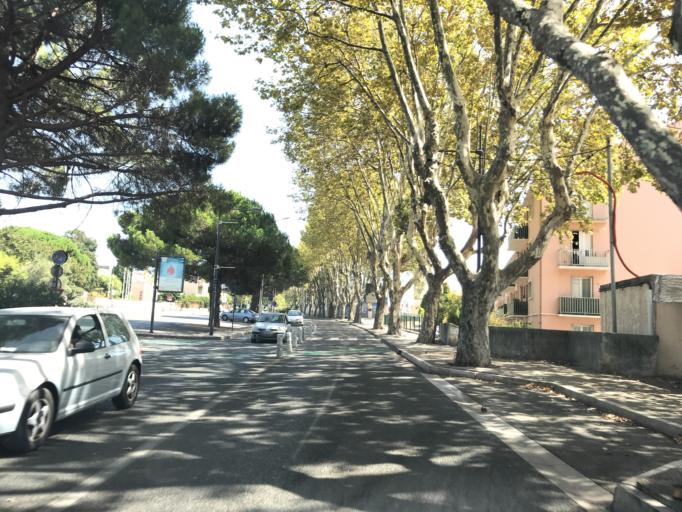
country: FR
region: Provence-Alpes-Cote d'Azur
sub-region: Departement du Var
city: Six-Fours-les-Plages
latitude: 43.0933
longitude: 5.8414
